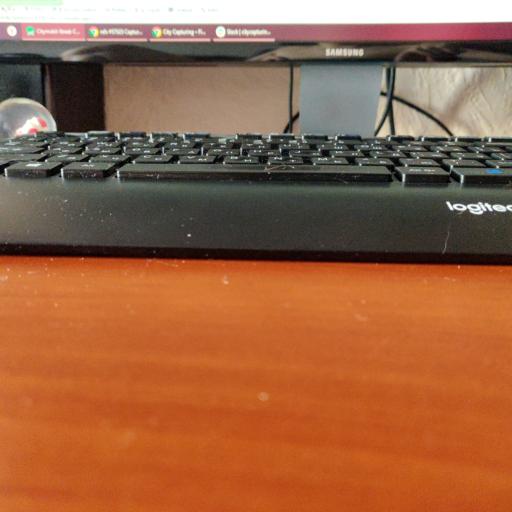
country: EE
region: Saare
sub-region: Kuressaare linn
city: Kuressaare
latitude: 58.5510
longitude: 22.5837
